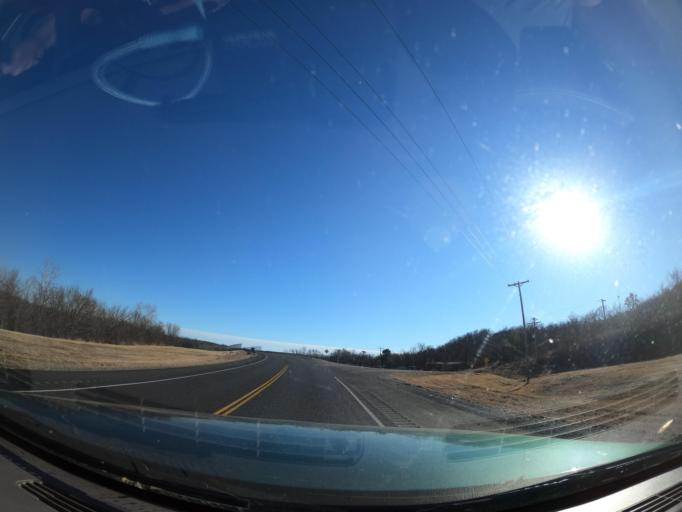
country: US
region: Oklahoma
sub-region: McIntosh County
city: Eufaula
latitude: 35.2703
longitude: -95.5852
